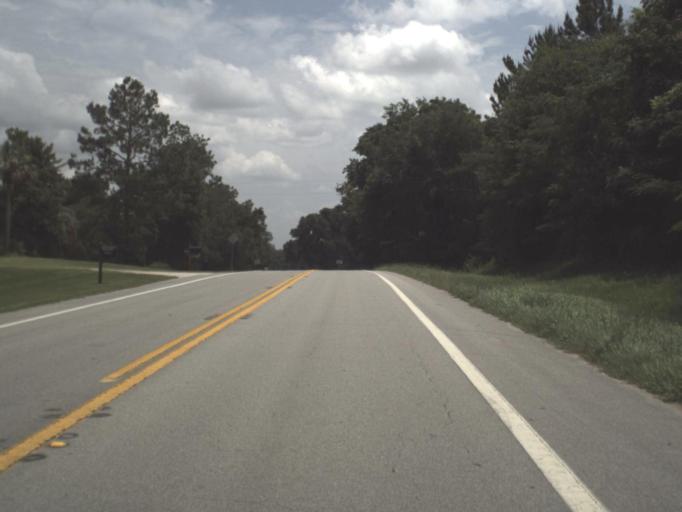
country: US
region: Florida
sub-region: Madison County
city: Madison
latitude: 30.5969
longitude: -83.4331
